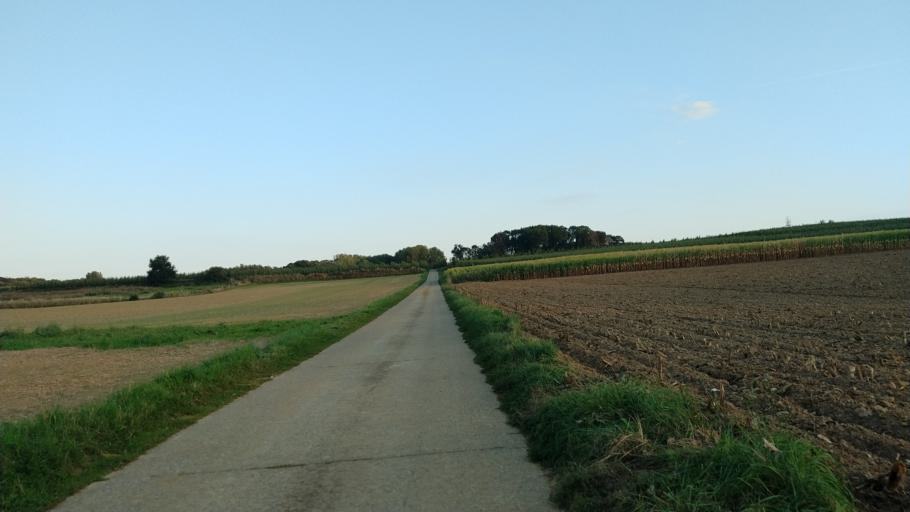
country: BE
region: Flanders
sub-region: Provincie Vlaams-Brabant
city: Lubbeek
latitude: 50.8914
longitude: 4.8175
